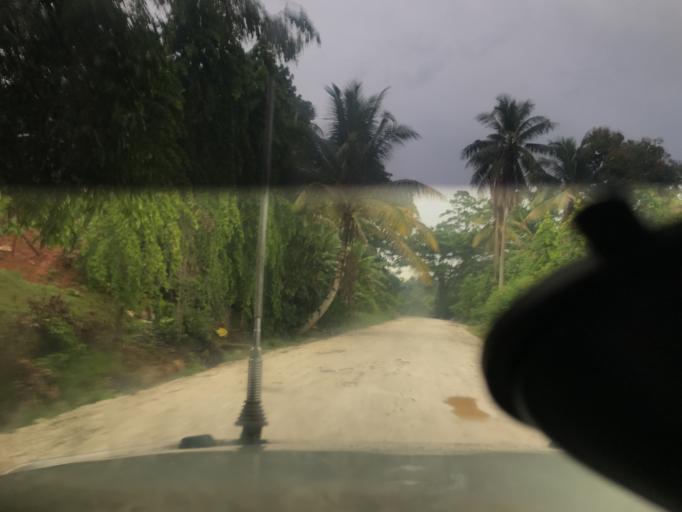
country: SB
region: Malaita
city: Auki
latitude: -8.8683
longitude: 160.7628
